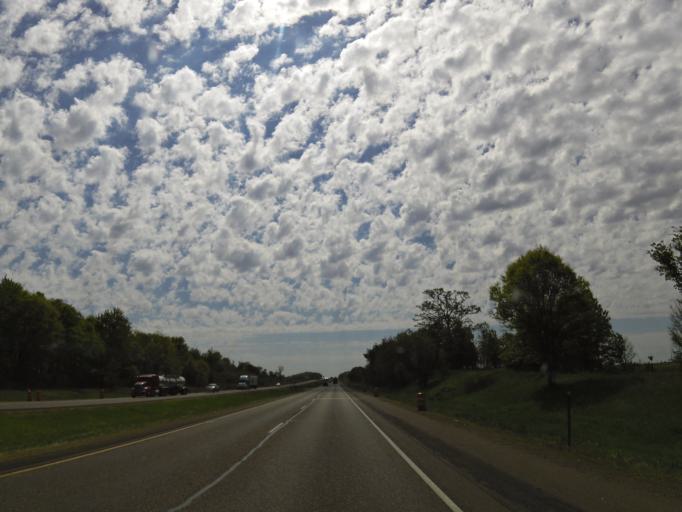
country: US
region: Wisconsin
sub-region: Dunn County
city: Colfax
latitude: 44.8914
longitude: -91.7419
